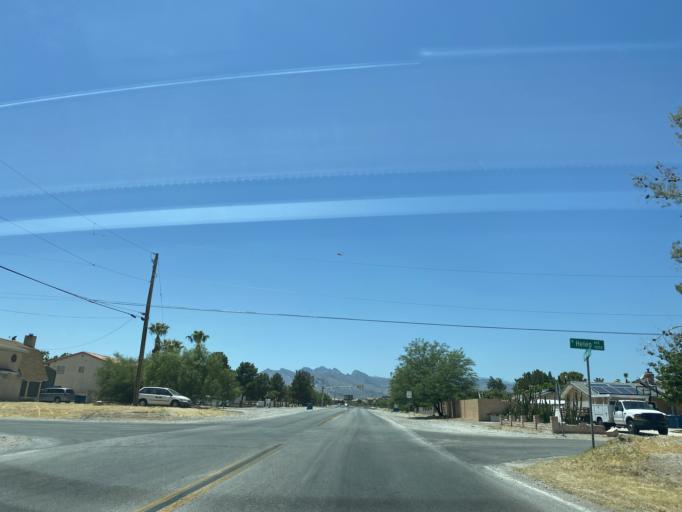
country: US
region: Nevada
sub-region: Clark County
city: Las Vegas
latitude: 36.2318
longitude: -115.2185
